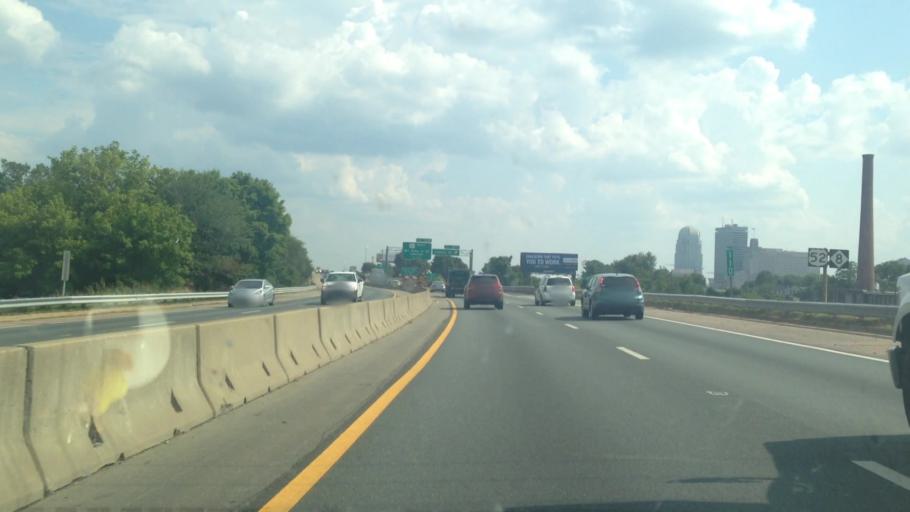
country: US
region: North Carolina
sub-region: Forsyth County
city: Winston-Salem
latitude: 36.1130
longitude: -80.2365
